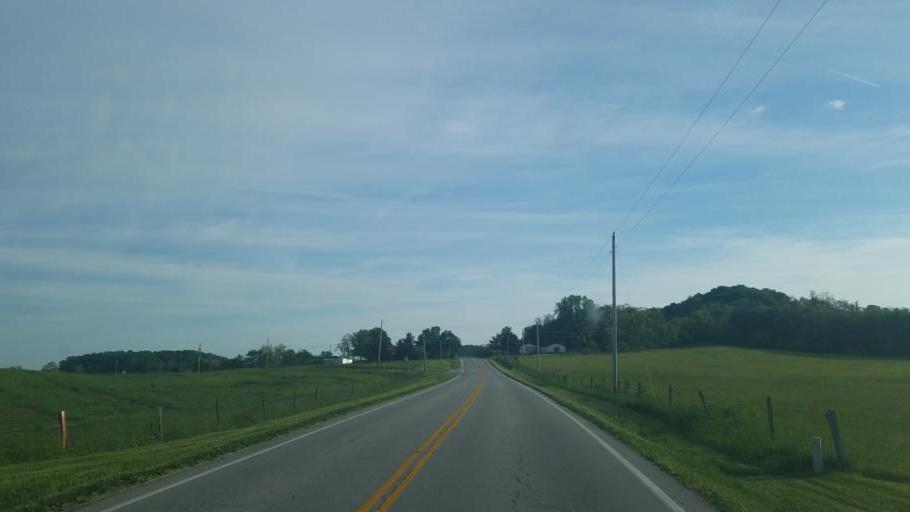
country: US
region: Ohio
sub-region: Ross County
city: Frankfort
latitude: 39.4199
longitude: -83.2684
